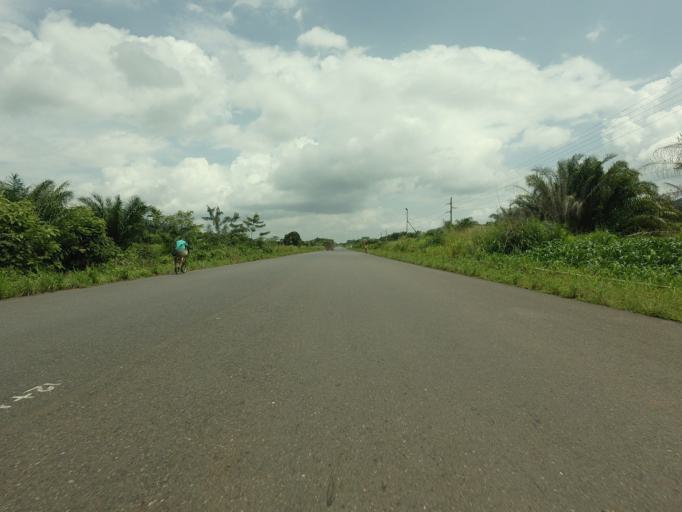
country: GH
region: Volta
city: Ho
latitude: 6.5106
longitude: 0.2147
